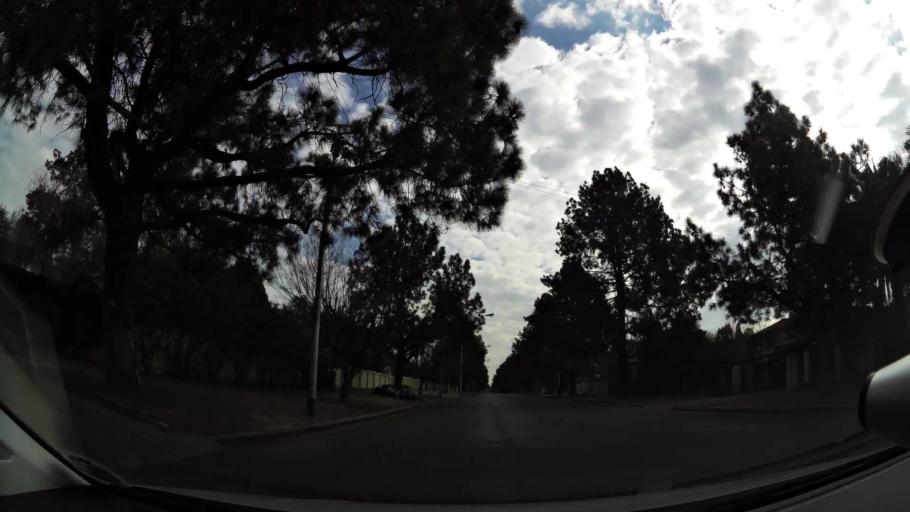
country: ZA
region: Orange Free State
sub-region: Mangaung Metropolitan Municipality
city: Bloemfontein
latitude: -29.0914
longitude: 26.2396
